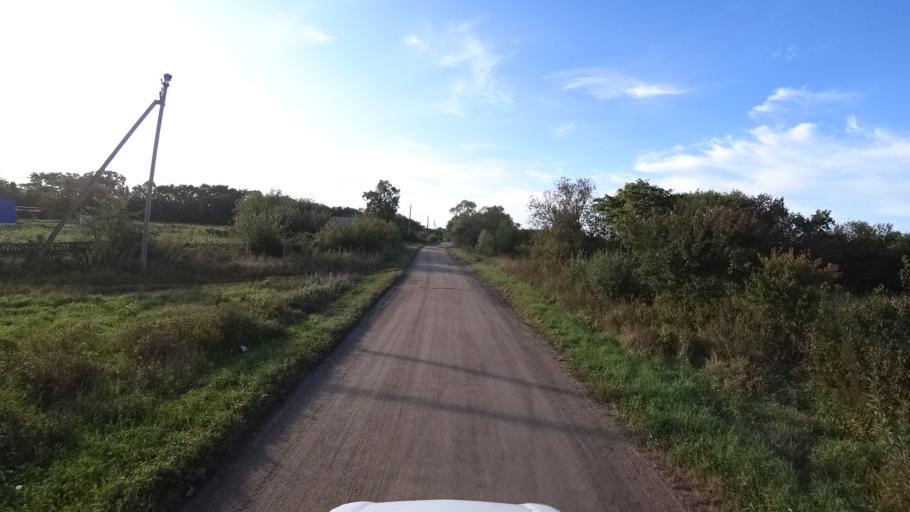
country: RU
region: Amur
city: Arkhara
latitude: 49.3613
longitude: 130.1251
